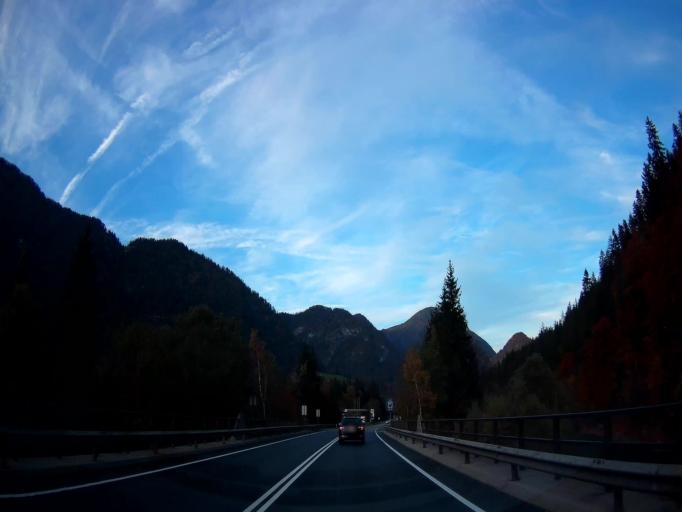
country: AT
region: Salzburg
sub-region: Politischer Bezirk Zell am See
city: Unken
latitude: 47.6510
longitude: 12.7379
